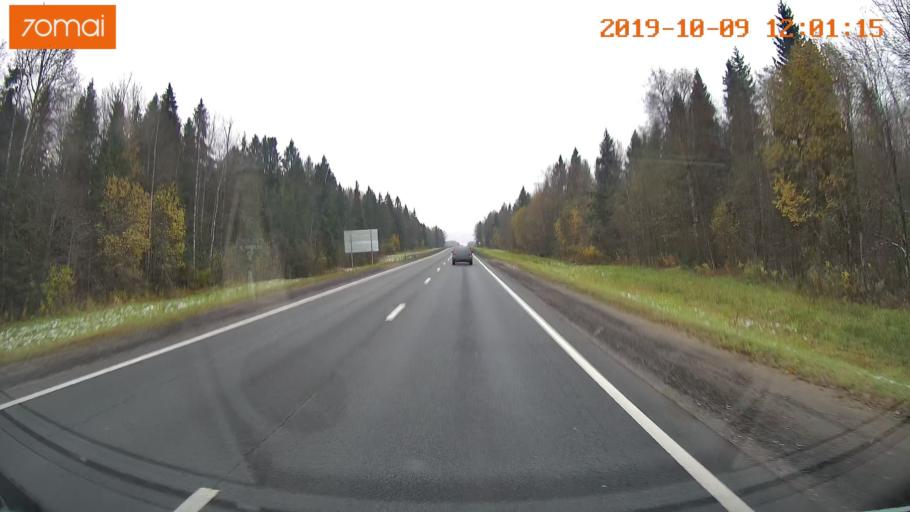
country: RU
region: Vologda
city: Gryazovets
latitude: 58.6901
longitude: 40.3026
